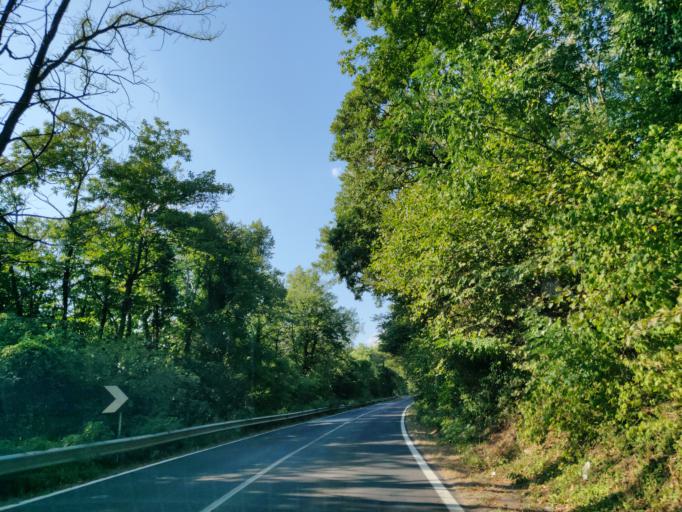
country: IT
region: Latium
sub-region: Provincia di Viterbo
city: Latera
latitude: 42.6192
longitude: 11.8393
